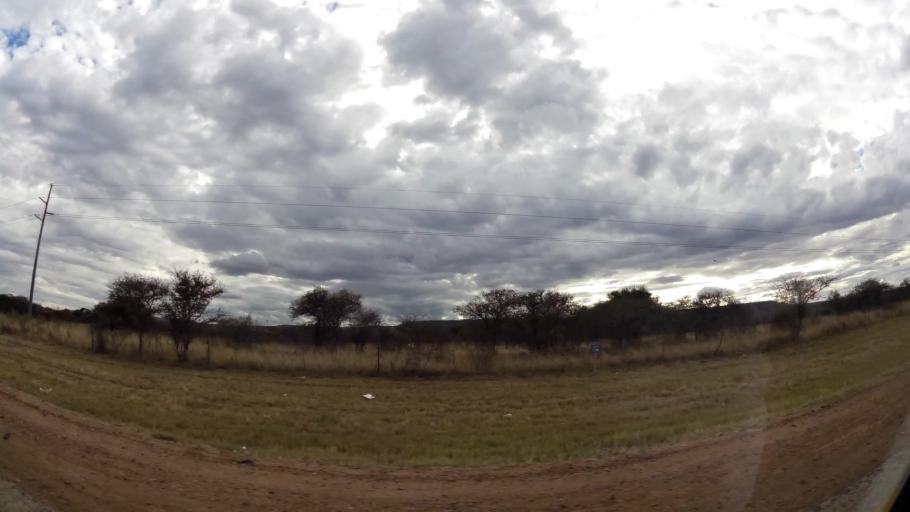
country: ZA
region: Limpopo
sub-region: Waterberg District Municipality
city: Modimolle
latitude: -24.5586
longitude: 28.6840
